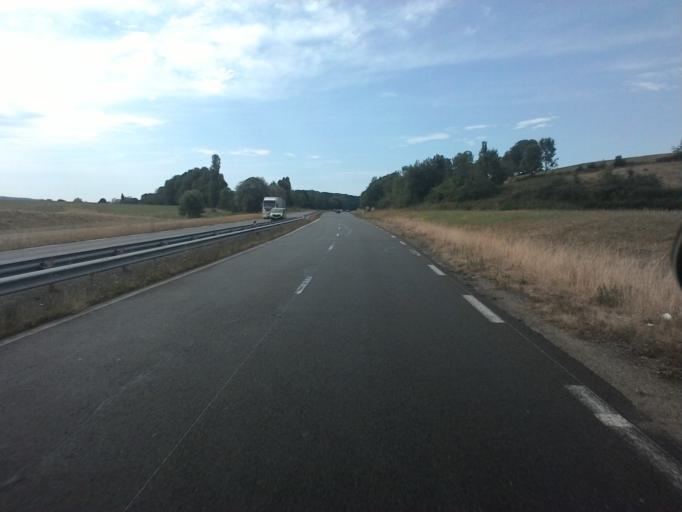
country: FR
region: Franche-Comte
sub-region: Departement du Jura
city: Lons-le-Saunier
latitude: 46.7253
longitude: 5.5575
